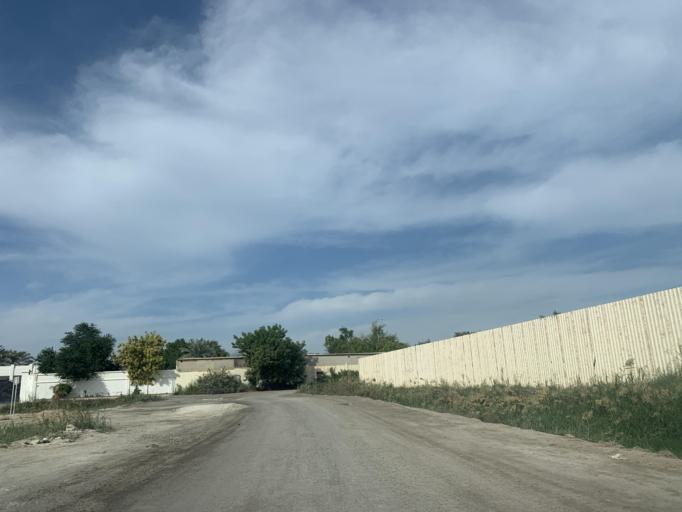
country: BH
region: Central Governorate
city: Madinat Hamad
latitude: 26.1195
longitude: 50.4697
